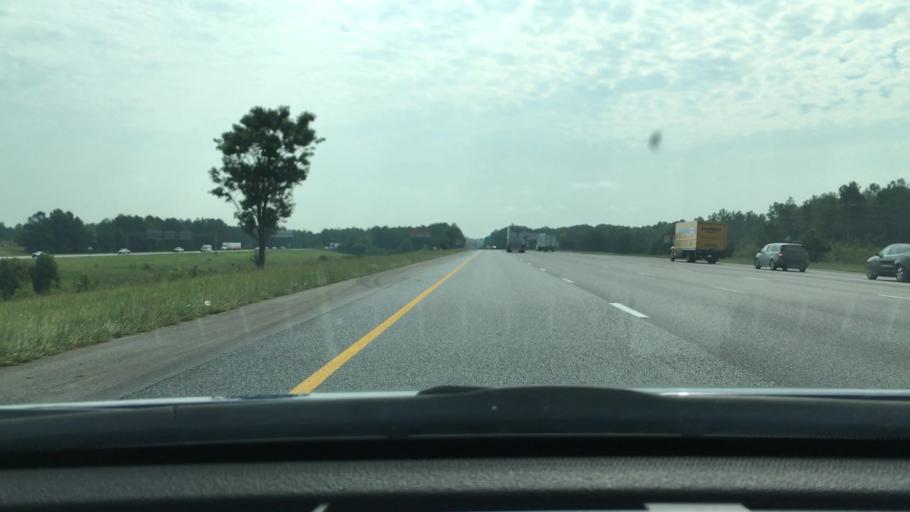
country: US
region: South Carolina
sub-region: Lexington County
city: Cayce
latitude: 33.9282
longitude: -81.0623
